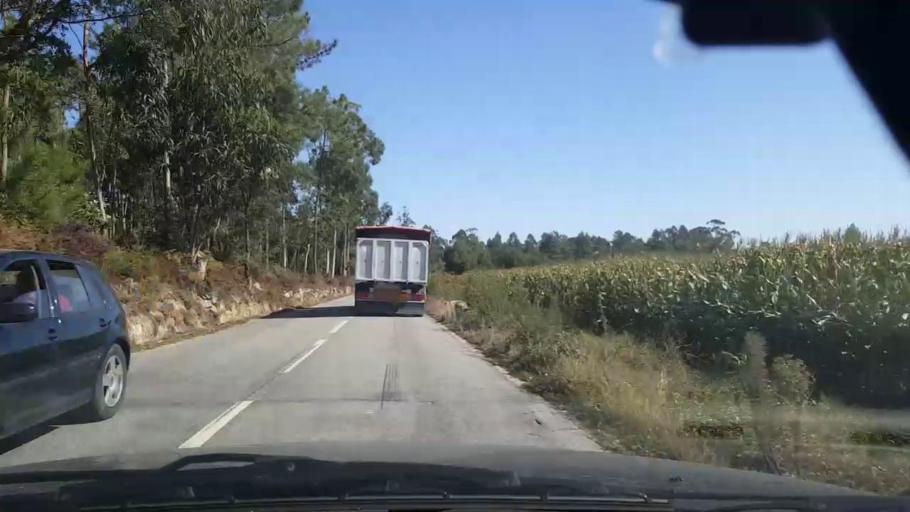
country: PT
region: Braga
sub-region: Vila Nova de Famalicao
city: Ribeirao
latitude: 41.3613
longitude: -8.6290
